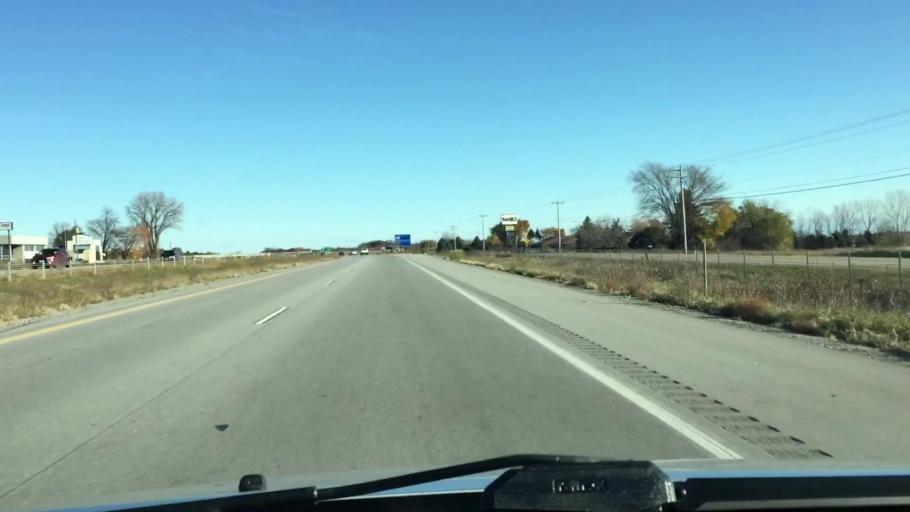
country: US
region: Wisconsin
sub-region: Brown County
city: Wrightstown
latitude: 44.3781
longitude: -88.1673
